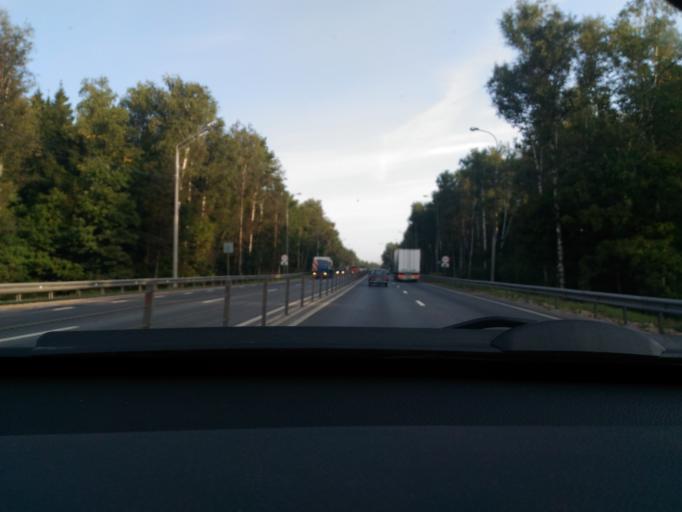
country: RU
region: Moskovskaya
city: Marfino
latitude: 56.0207
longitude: 37.5448
